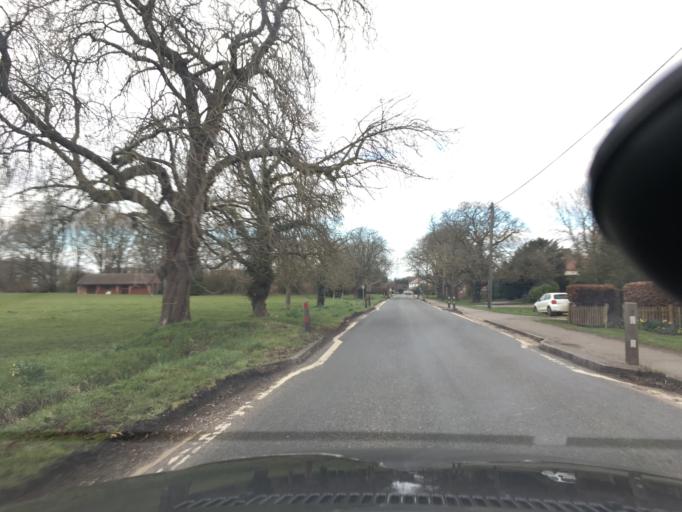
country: GB
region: England
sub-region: Hampshire
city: Old Basing
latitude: 51.3176
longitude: -1.0262
